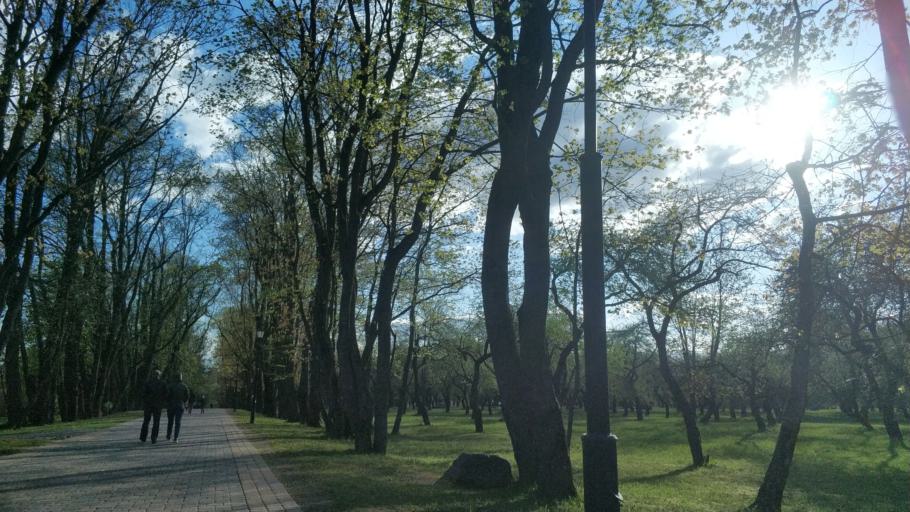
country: BY
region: Minsk
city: Minsk
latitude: 53.8544
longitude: 27.5798
